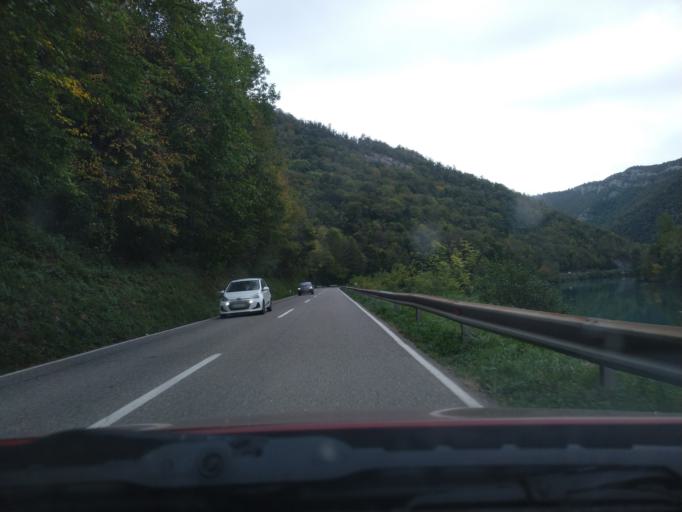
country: SI
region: Kanal
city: Deskle
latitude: 46.0254
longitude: 13.6053
